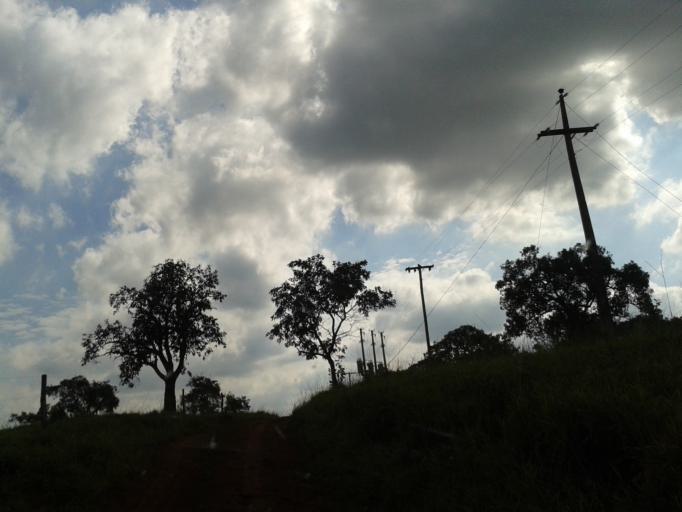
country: BR
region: Minas Gerais
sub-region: Campina Verde
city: Campina Verde
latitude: -19.3937
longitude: -49.6875
